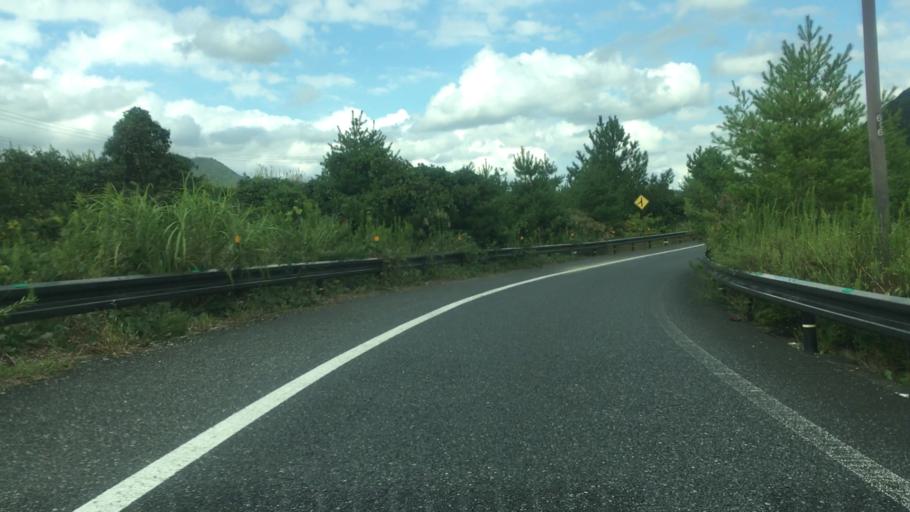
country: JP
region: Kyoto
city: Fukuchiyama
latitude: 35.1623
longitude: 135.0444
